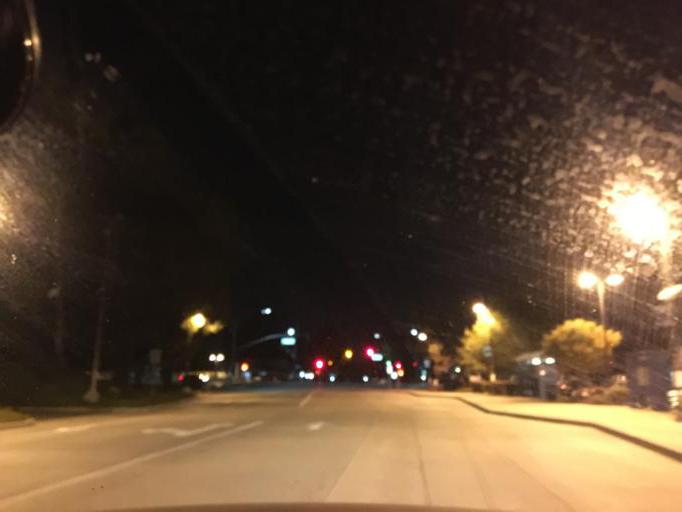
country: US
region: California
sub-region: Santa Clara County
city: Alum Rock
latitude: 37.3825
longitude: -121.8544
